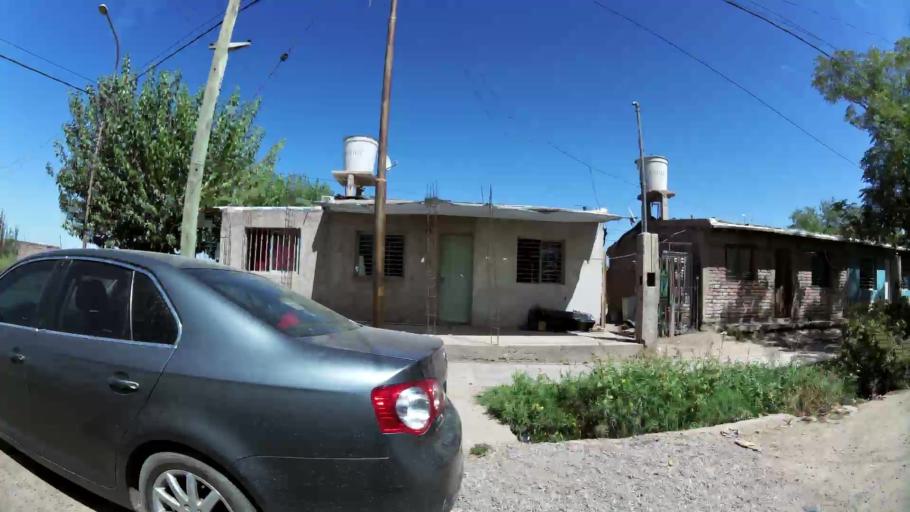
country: AR
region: Mendoza
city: Villa Nueva
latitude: -32.8762
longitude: -68.7867
